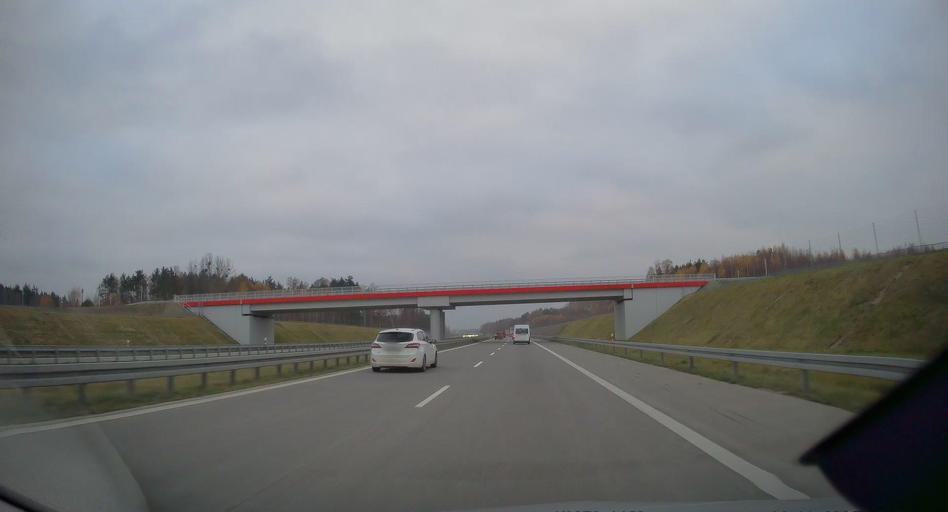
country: PL
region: Silesian Voivodeship
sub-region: Powiat czestochowski
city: Starcza
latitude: 50.6554
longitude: 19.0399
